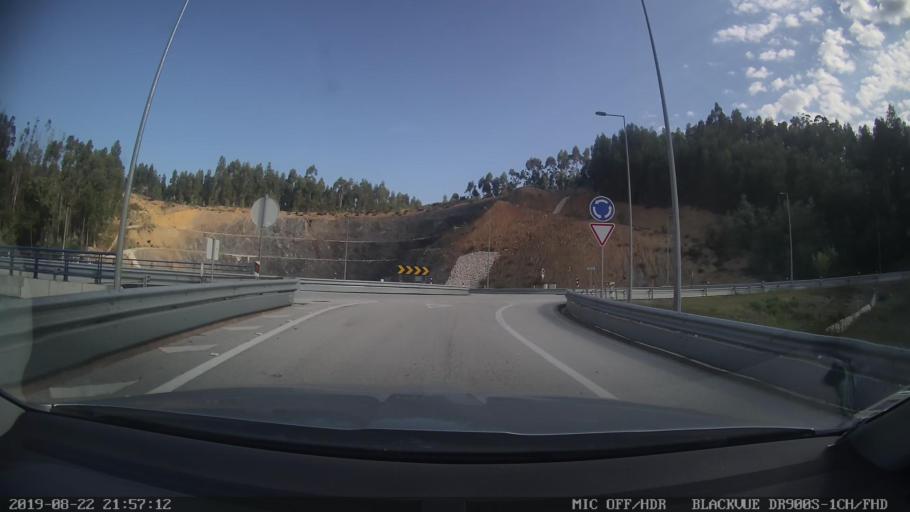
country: PT
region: Coimbra
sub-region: Coimbra
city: Coimbra
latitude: 40.1825
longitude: -8.3794
